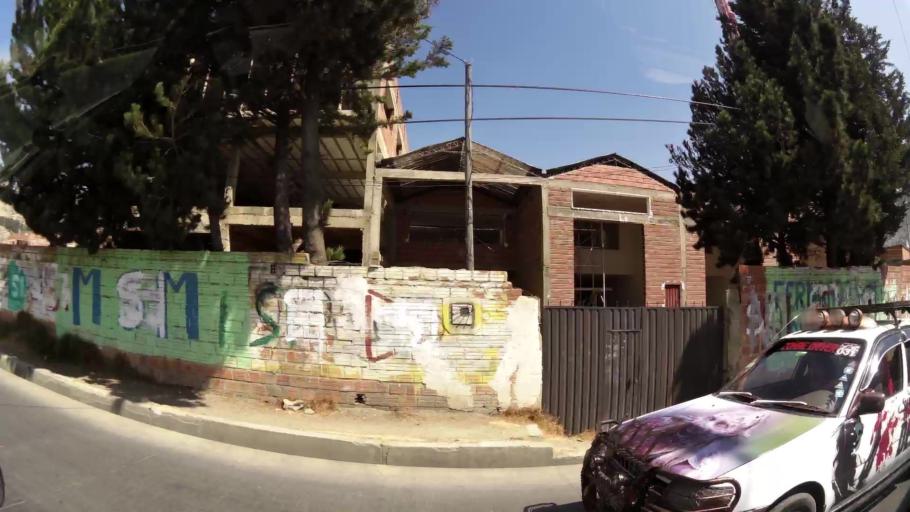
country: BO
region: La Paz
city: La Paz
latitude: -16.5297
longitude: -68.1271
